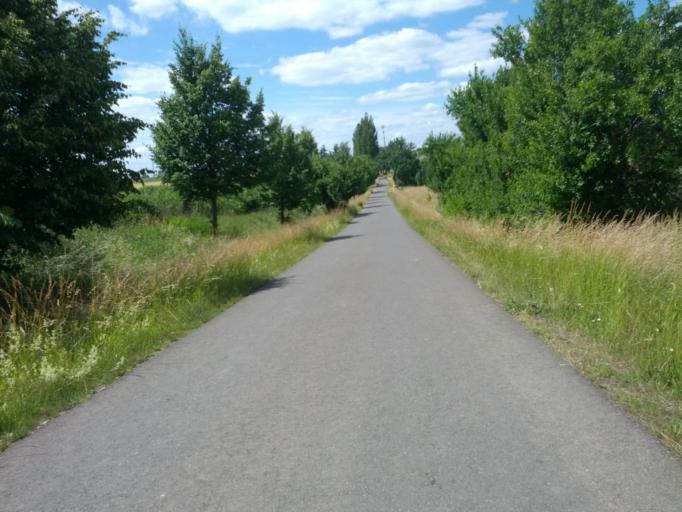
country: DE
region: Thuringia
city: Bischofroda
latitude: 51.0129
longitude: 10.3570
